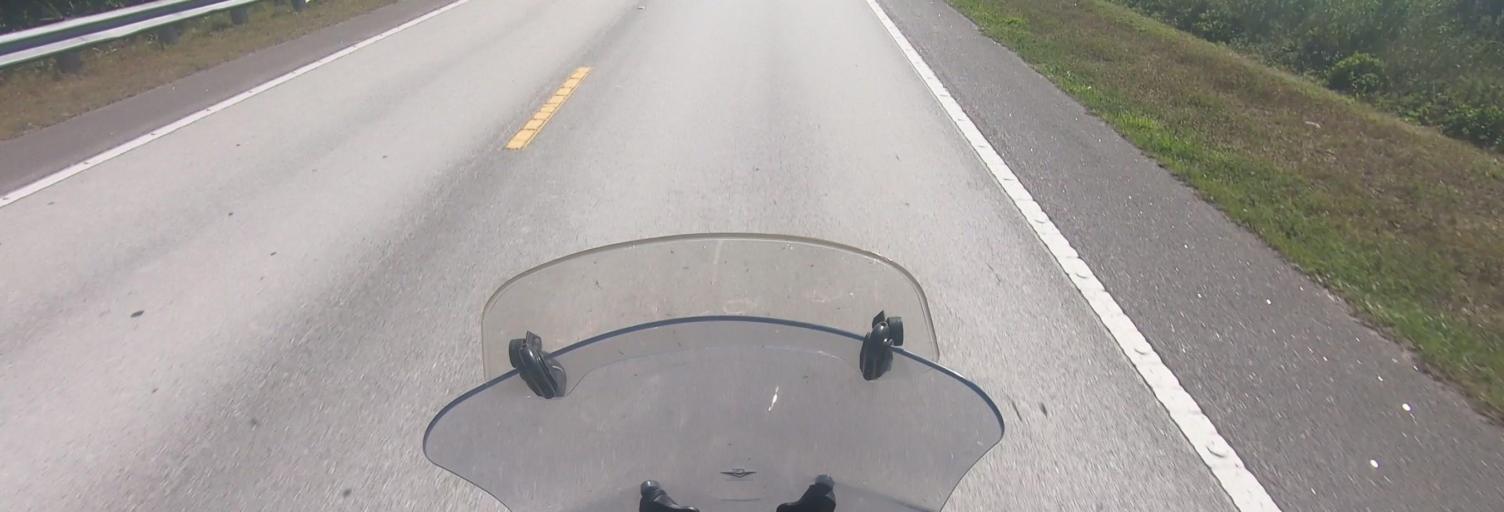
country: US
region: Florida
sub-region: Collier County
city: Marco
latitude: 25.8749
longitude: -81.2161
